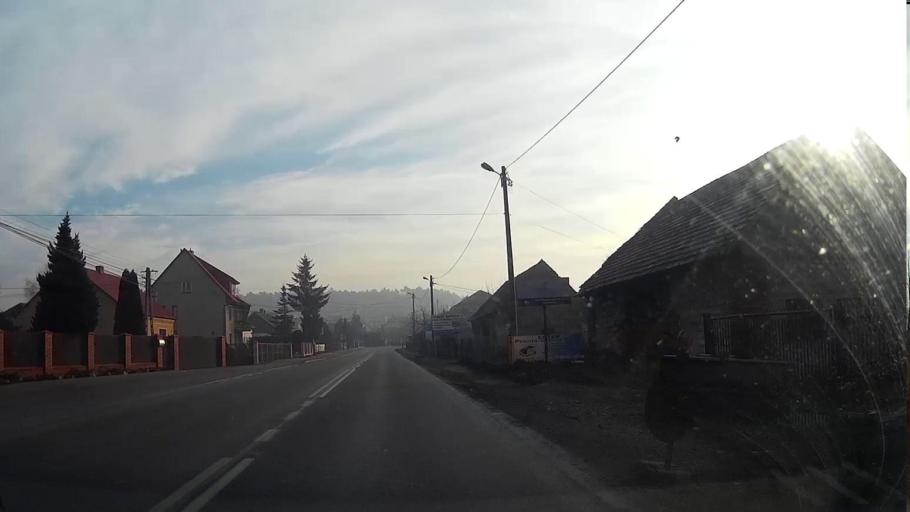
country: PL
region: Lesser Poland Voivodeship
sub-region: Powiat krakowski
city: Kryspinow
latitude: 50.0436
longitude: 19.7944
